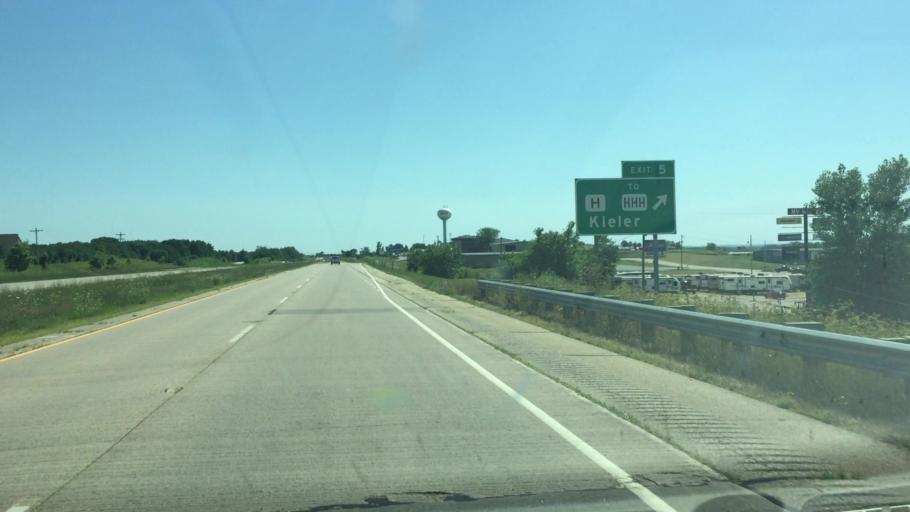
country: US
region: Wisconsin
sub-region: Grant County
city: Dickeyville
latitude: 42.5936
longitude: -90.5999
